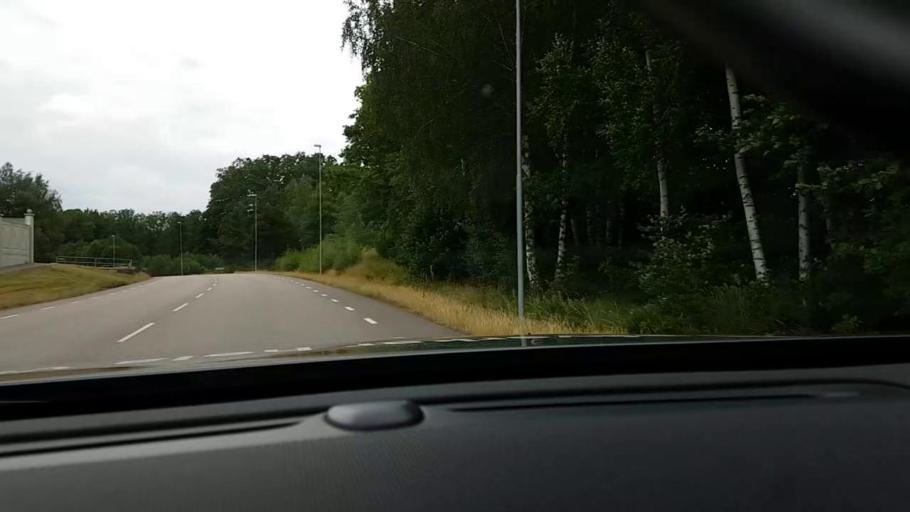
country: SE
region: Skane
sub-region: Hassleholms Kommun
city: Hassleholm
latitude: 56.1681
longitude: 13.7437
